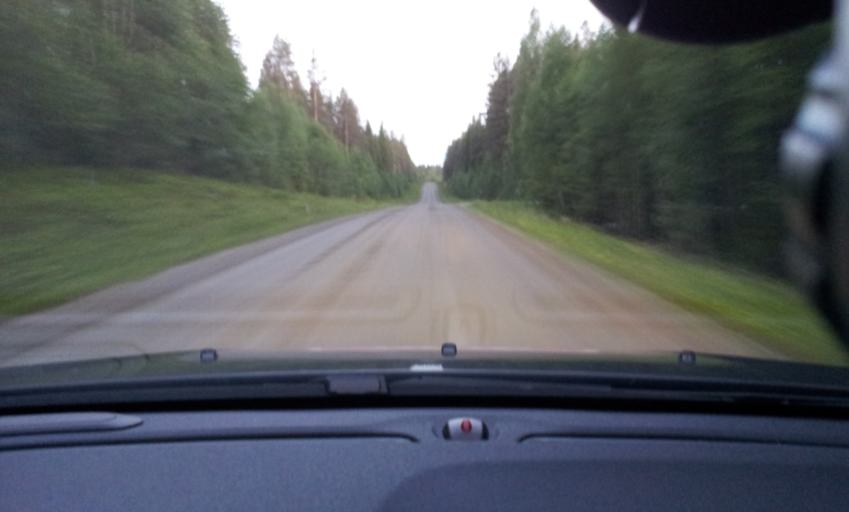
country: SE
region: Vaesternorrland
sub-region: Ange Kommun
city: Fransta
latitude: 62.8647
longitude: 16.0458
